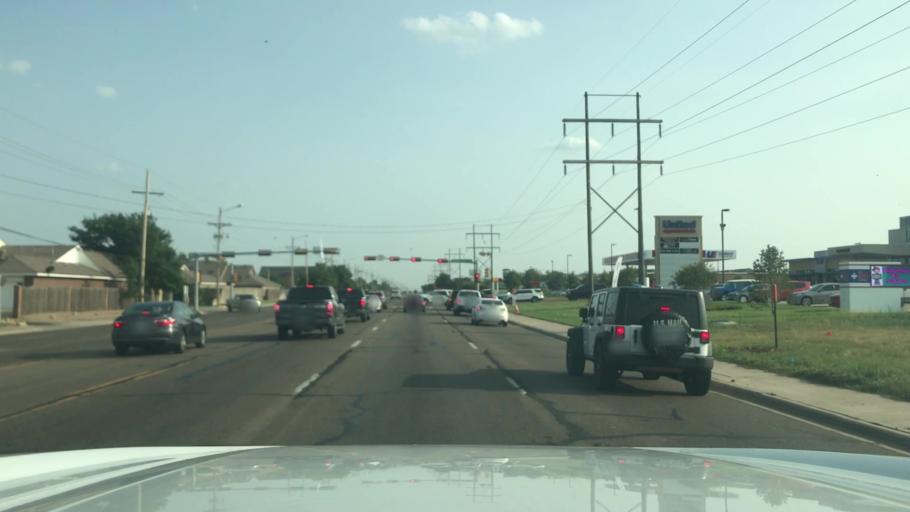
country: US
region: Texas
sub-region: Potter County
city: Amarillo
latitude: 35.1718
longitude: -101.9383
